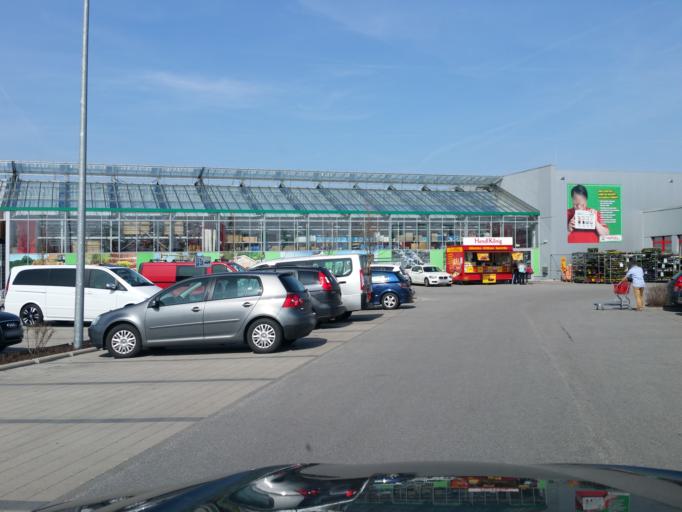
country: DE
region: Bavaria
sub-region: Upper Bavaria
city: Moosburg
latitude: 48.4719
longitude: 11.9659
